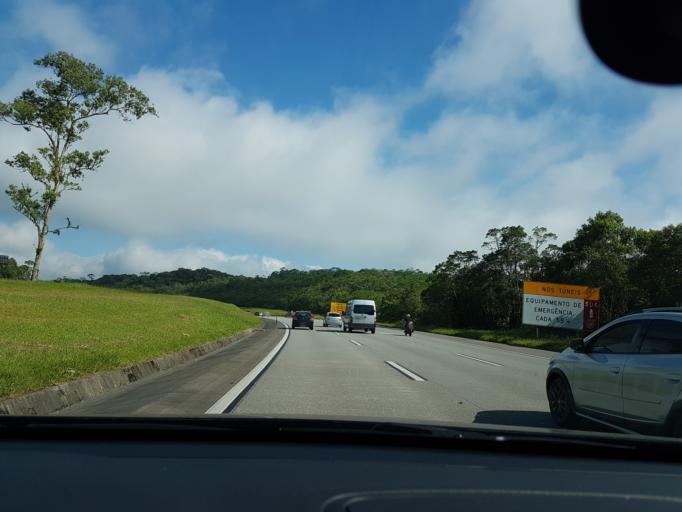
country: BR
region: Sao Paulo
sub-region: Cubatao
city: Cubatao
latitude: -23.9250
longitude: -46.5548
